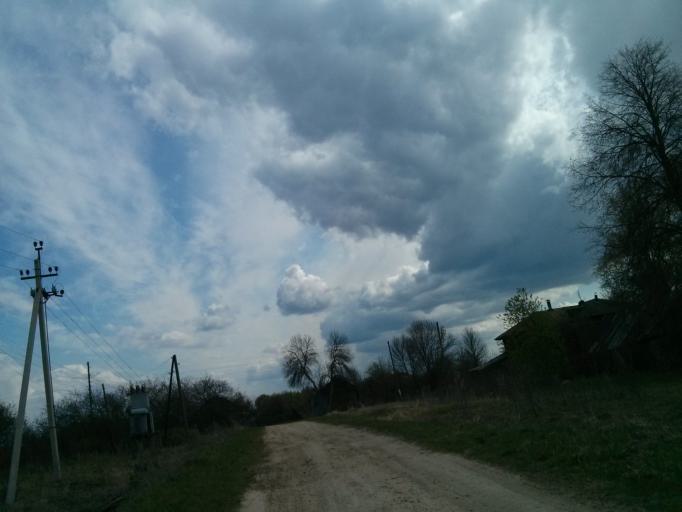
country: RU
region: Nizjnij Novgorod
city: Shimorskoye
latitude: 55.3054
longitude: 41.8415
